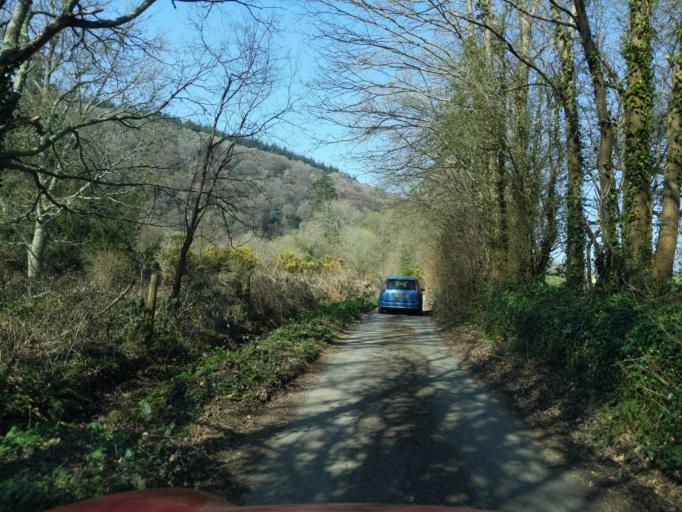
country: GB
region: England
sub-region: Devon
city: Bere Alston
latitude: 50.4606
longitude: -4.1546
